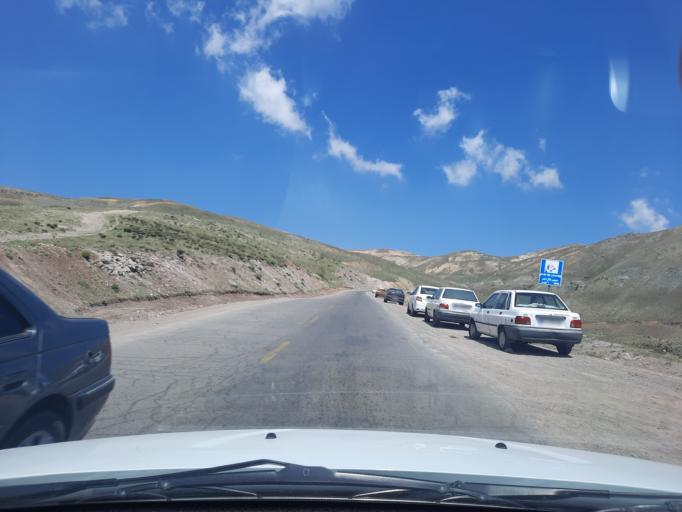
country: IR
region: Qazvin
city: Qazvin
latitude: 36.3744
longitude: 50.2067
